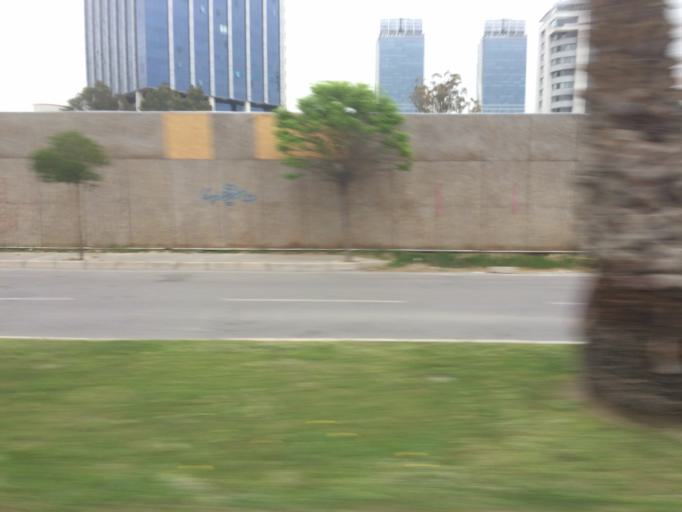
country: TR
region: Izmir
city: Izmir
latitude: 38.4523
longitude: 27.1692
